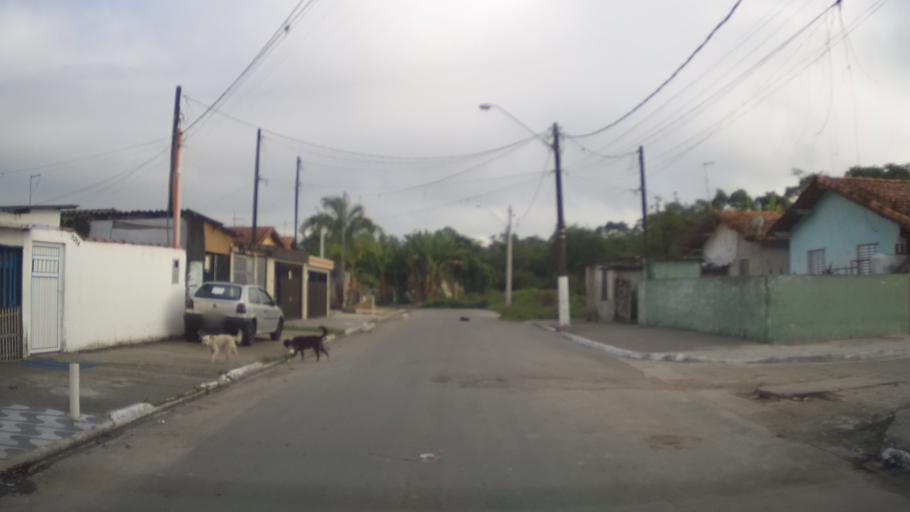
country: BR
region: Sao Paulo
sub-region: Praia Grande
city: Praia Grande
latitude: -24.0132
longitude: -46.4674
